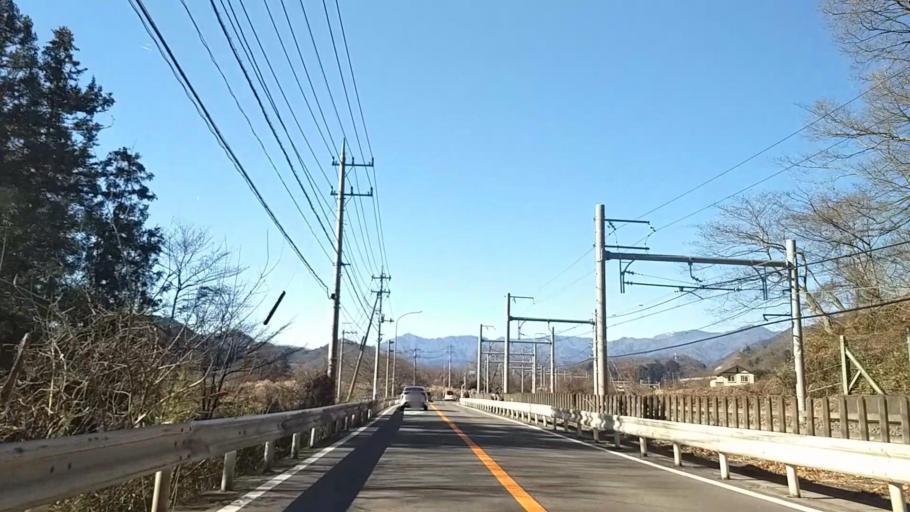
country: JP
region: Yamanashi
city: Otsuki
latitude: 35.6043
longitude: 139.0188
